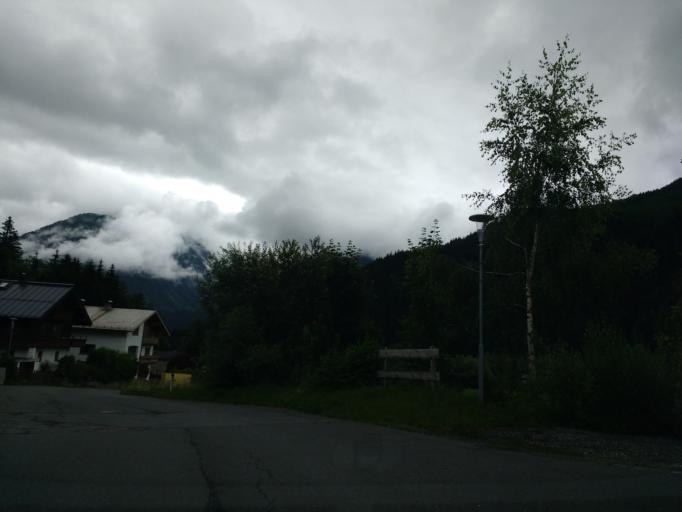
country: AT
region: Salzburg
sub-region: Politischer Bezirk Zell am See
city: Wald im Pinzgau
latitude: 47.2466
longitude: 12.2303
